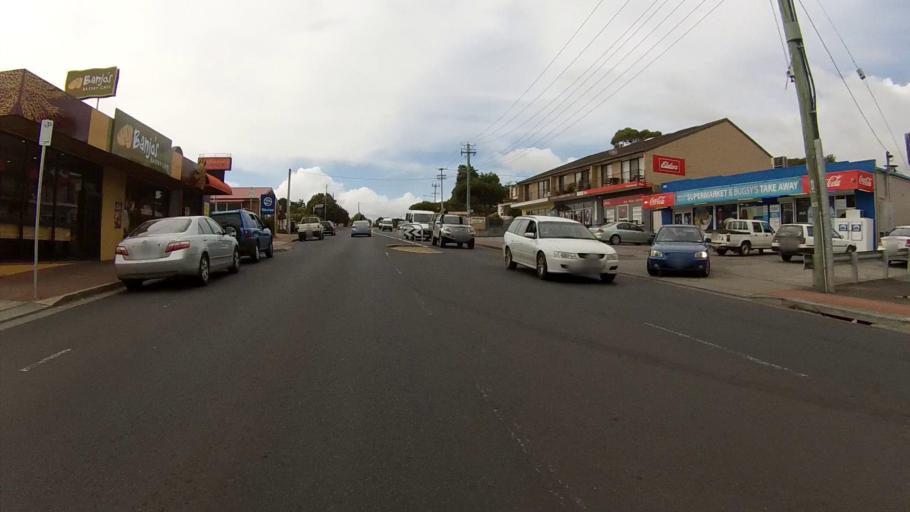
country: AU
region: Tasmania
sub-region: Kingborough
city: Margate
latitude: -43.0265
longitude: 147.2614
